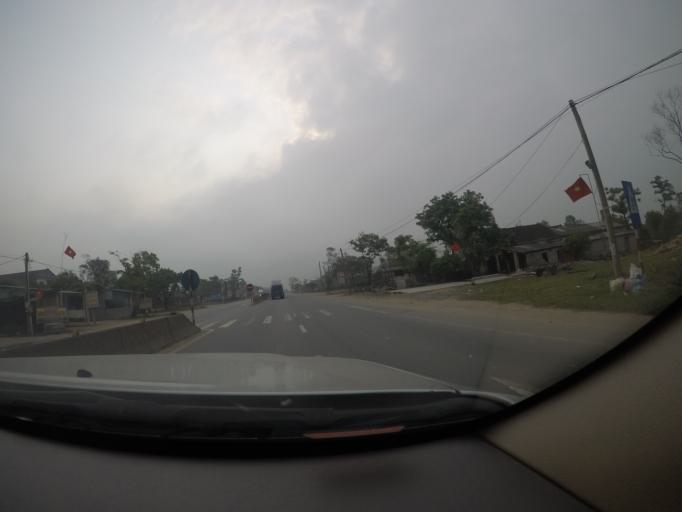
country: VN
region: Ha Tinh
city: Cam Xuyen
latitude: 18.2039
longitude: 106.1384
